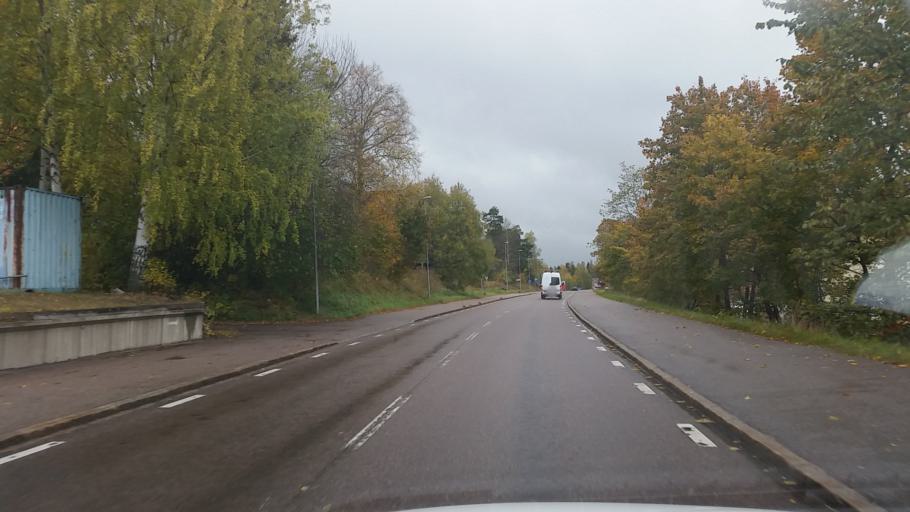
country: SE
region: Gaevleborg
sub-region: Sandvikens Kommun
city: Jarbo
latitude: 60.5812
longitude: 16.5271
